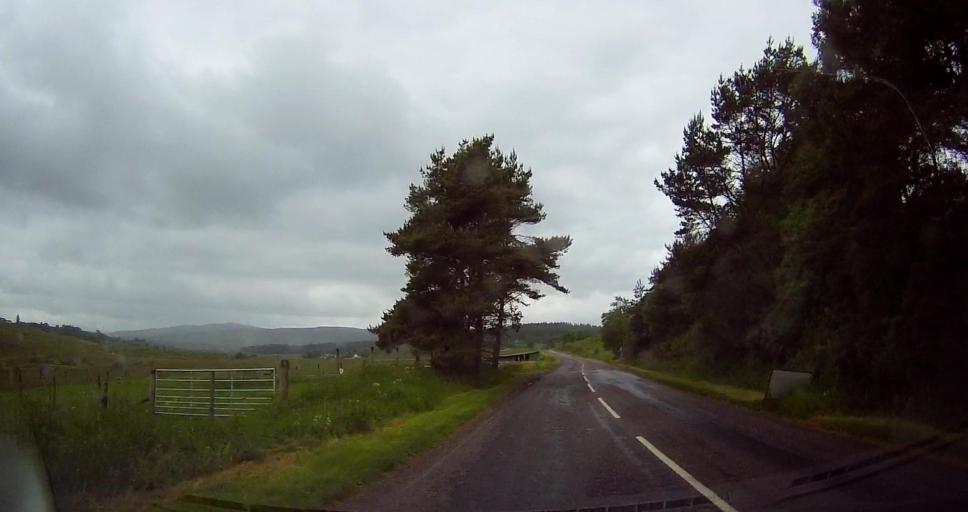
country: GB
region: Scotland
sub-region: Highland
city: Alness
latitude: 58.0177
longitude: -4.3579
